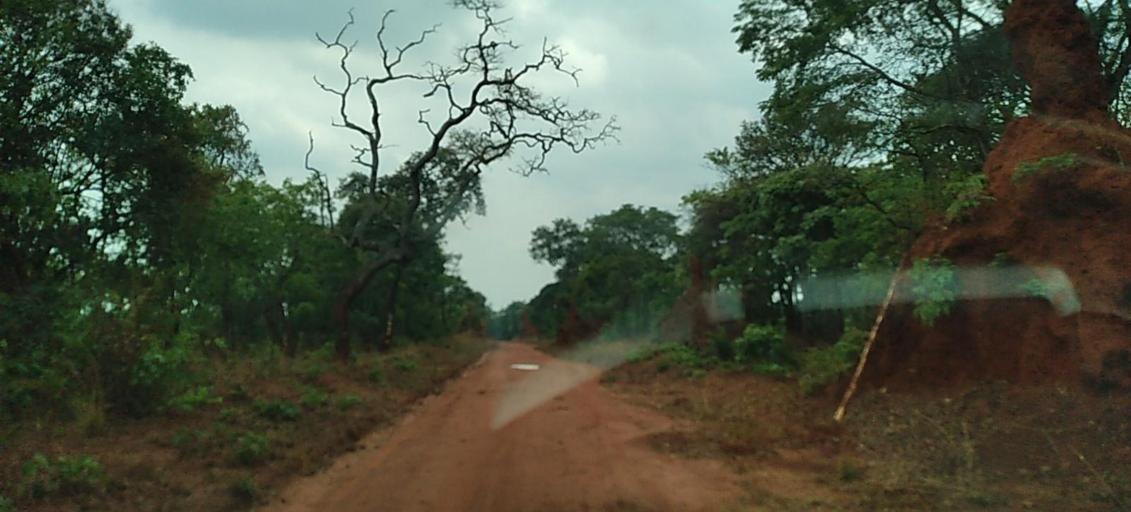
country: ZM
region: North-Western
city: Mwinilunga
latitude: -11.5446
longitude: 24.7784
